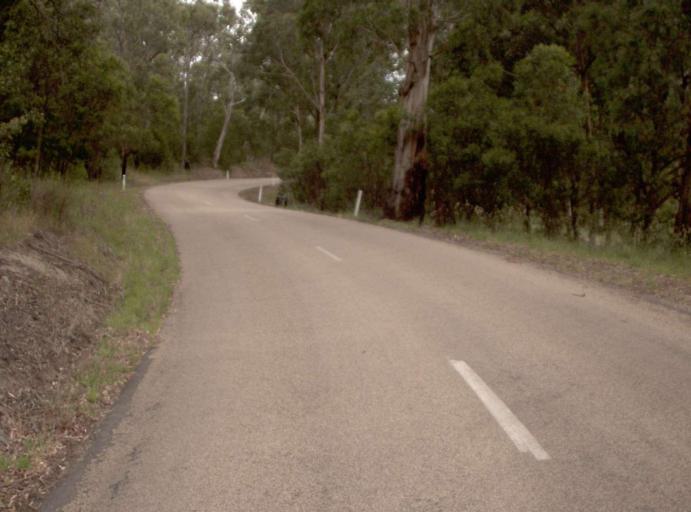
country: AU
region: Victoria
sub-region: East Gippsland
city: Bairnsdale
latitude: -37.7199
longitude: 147.5938
